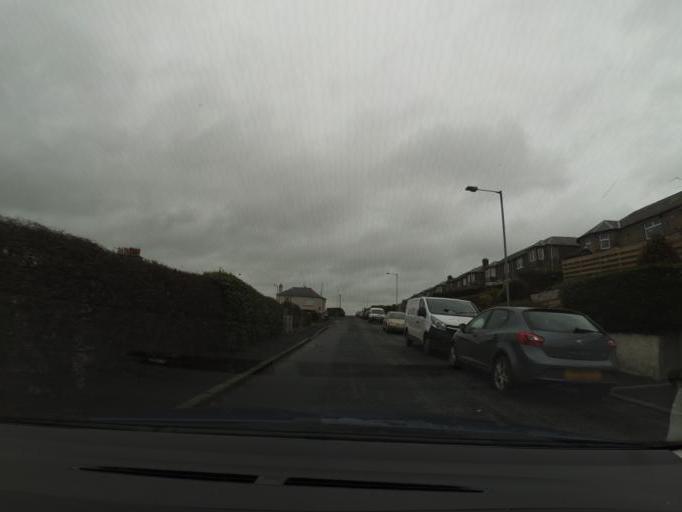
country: GB
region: Scotland
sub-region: The Scottish Borders
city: Hawick
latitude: 55.4237
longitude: -2.7796
